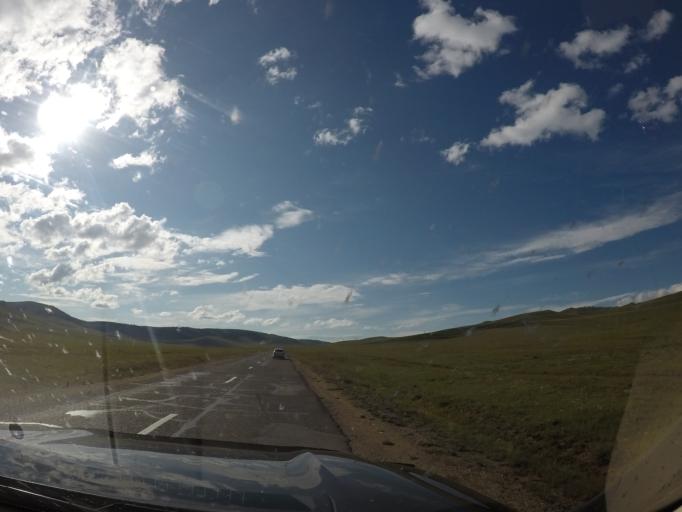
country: MN
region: Hentiy
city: Modot
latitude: 47.7669
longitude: 108.8886
